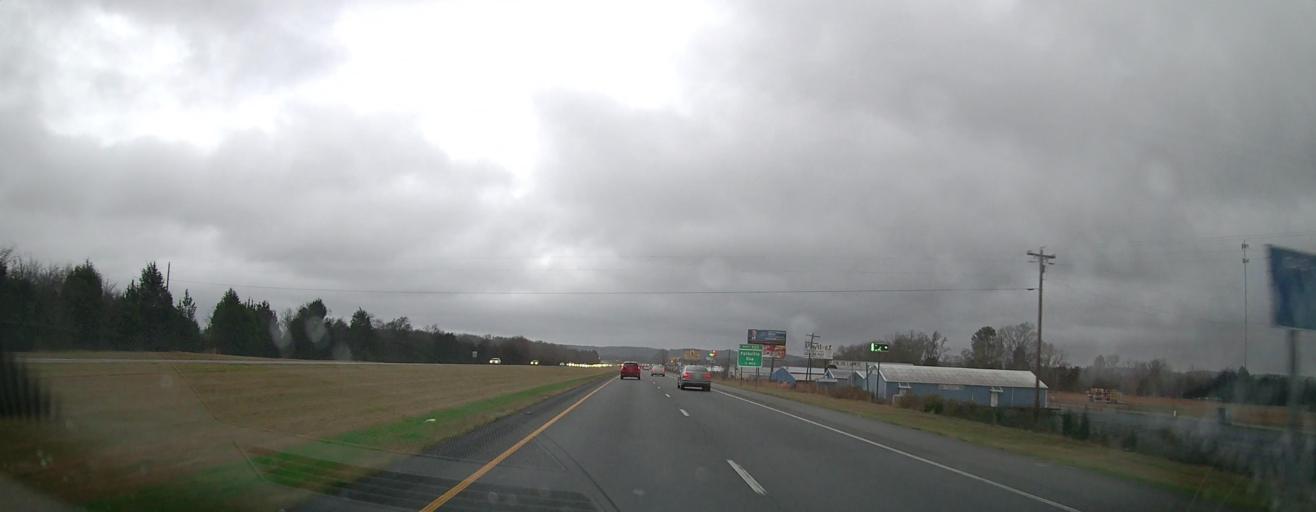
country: US
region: Alabama
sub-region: Morgan County
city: Falkville
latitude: 34.3818
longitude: -86.8937
